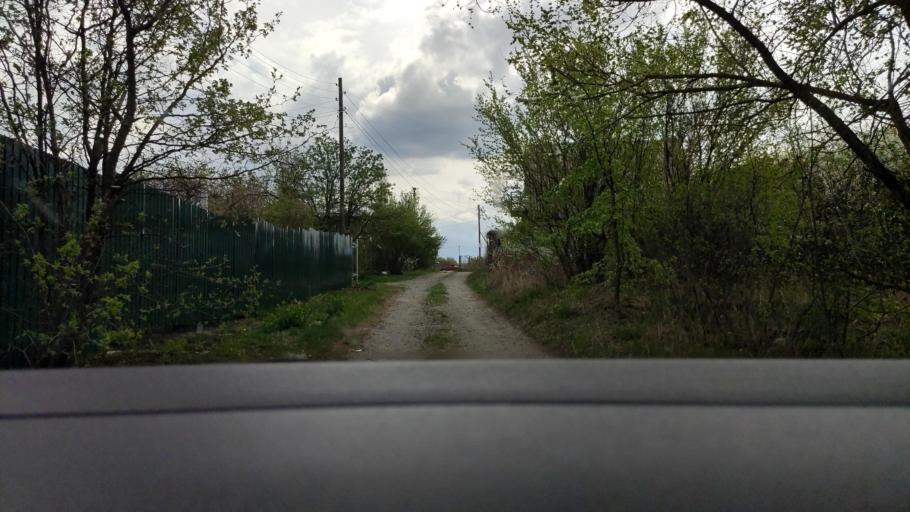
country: RU
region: Voronezj
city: Semiluki
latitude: 51.7806
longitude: 38.9996
